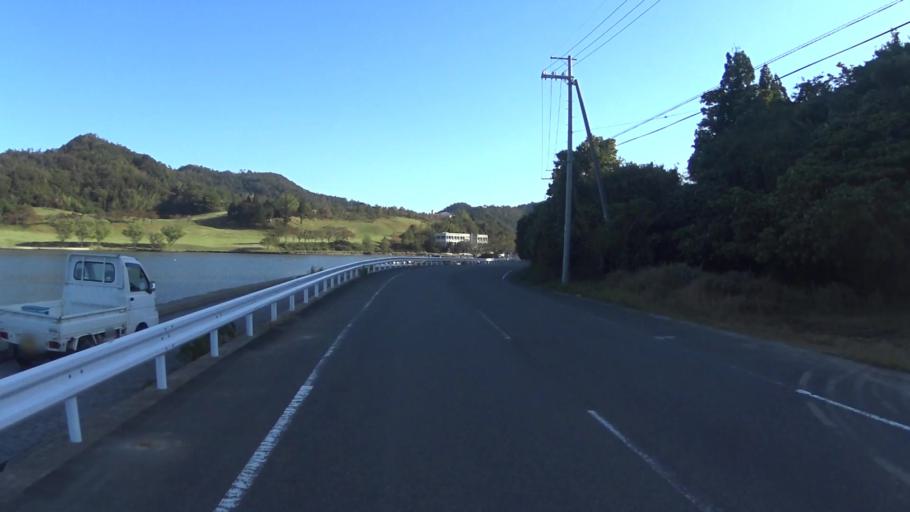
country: JP
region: Hyogo
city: Toyooka
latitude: 35.6306
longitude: 134.8877
